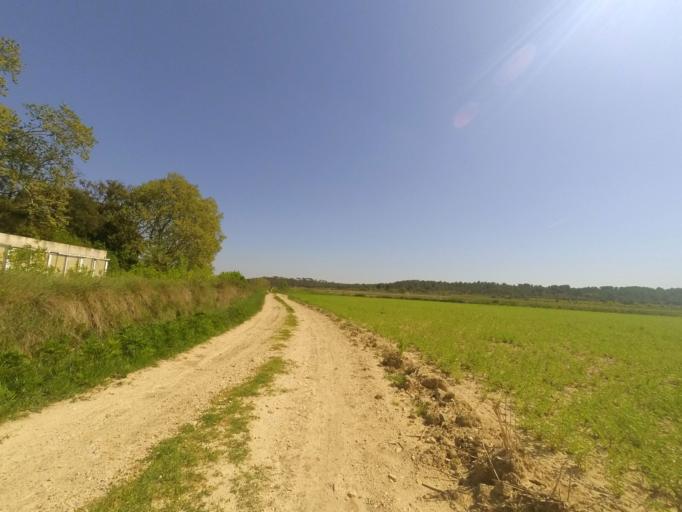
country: FR
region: Languedoc-Roussillon
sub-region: Departement du Gard
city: Congenies
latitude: 43.7703
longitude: 4.1820
